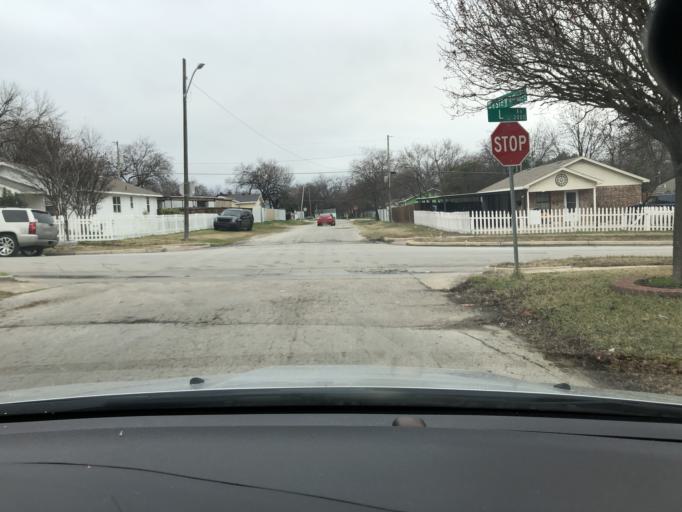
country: US
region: Texas
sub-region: Tarrant County
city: Fort Worth
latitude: 32.7255
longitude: -97.2811
